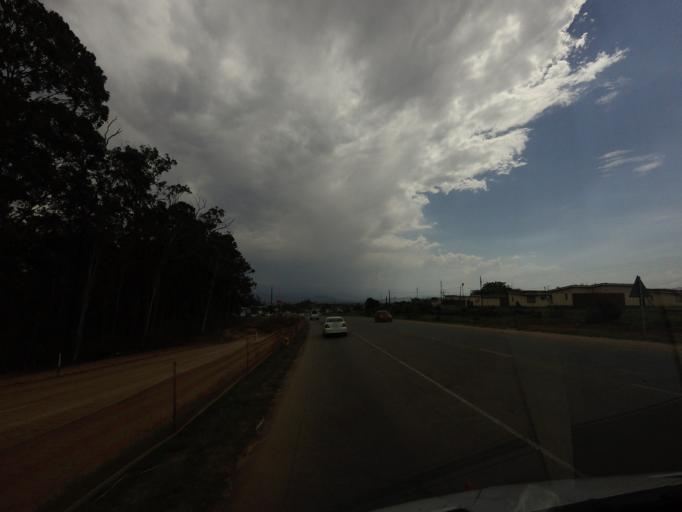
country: SZ
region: Manzini
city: Manzini
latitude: -26.4884
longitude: 31.4148
